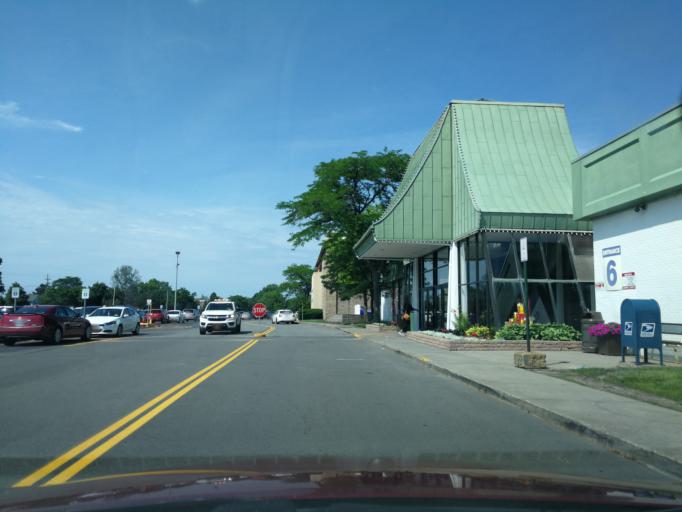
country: US
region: New York
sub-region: Monroe County
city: Greece
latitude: 43.2056
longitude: -77.6948
